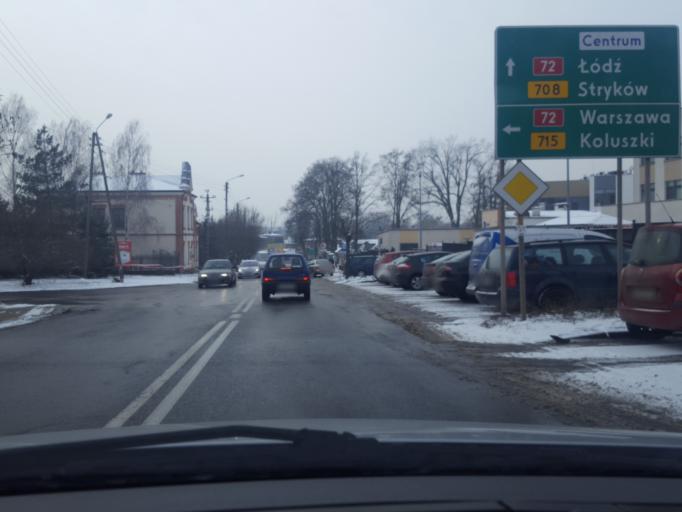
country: PL
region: Lodz Voivodeship
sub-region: Powiat brzezinski
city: Brzeziny
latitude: 51.8061
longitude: 19.7561
